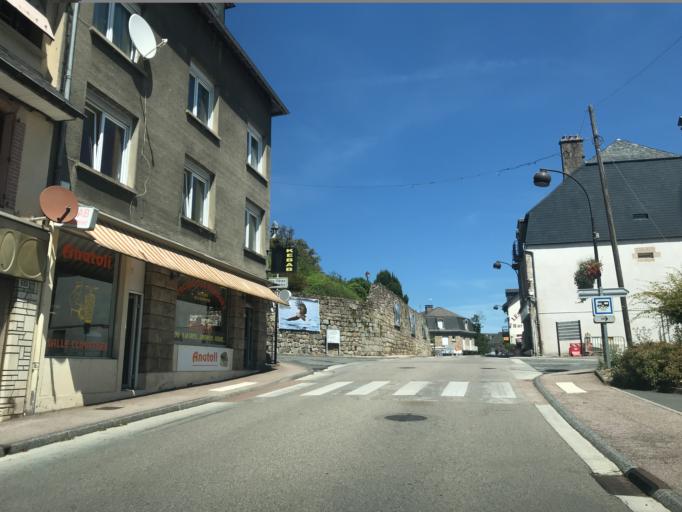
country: FR
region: Limousin
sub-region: Departement de la Correze
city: Egletons
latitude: 45.4049
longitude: 2.0460
